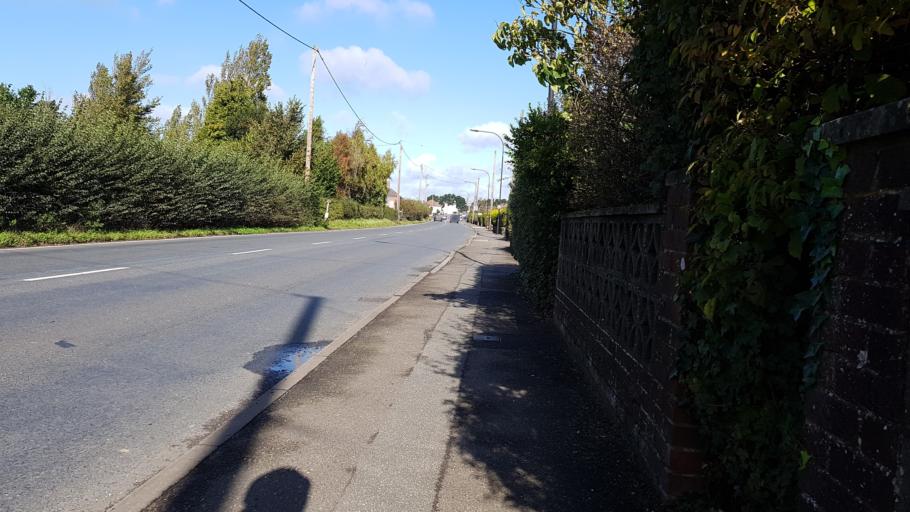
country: GB
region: England
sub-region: Isle of Wight
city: Northwood
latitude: 50.7355
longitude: -1.3066
